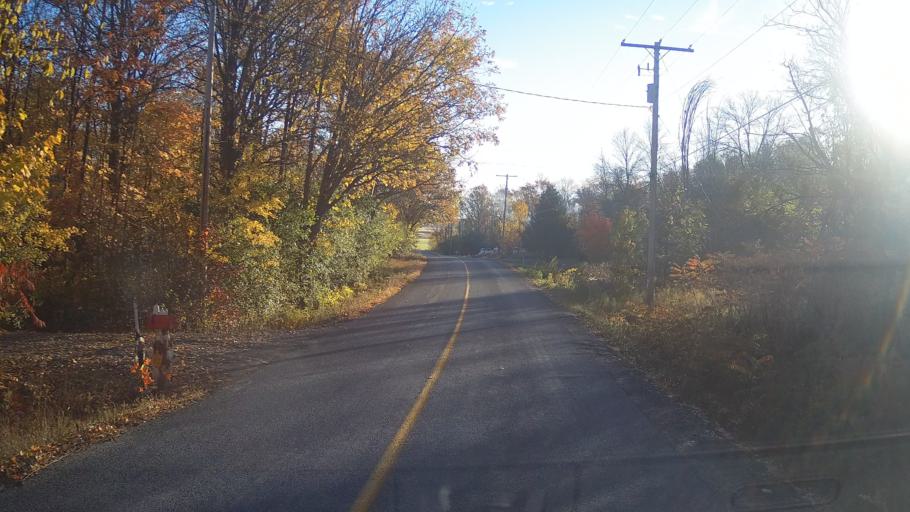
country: CA
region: Ontario
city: Arnprior
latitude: 45.3448
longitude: -76.3233
